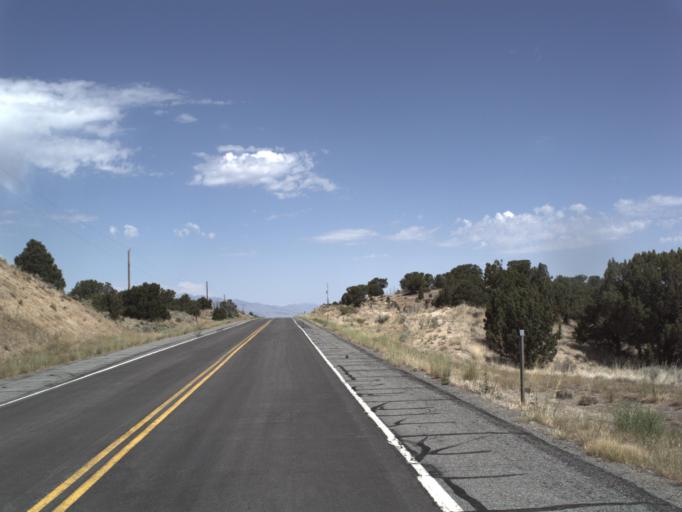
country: US
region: Utah
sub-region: Utah County
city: Eagle Mountain
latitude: 40.0296
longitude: -112.2834
